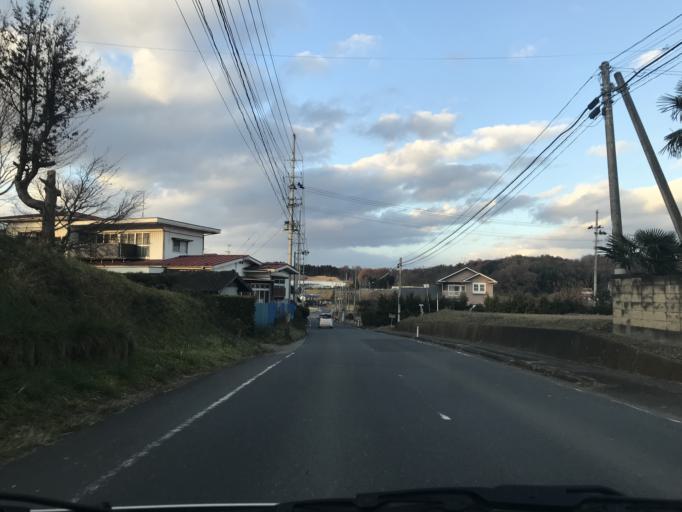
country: JP
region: Miyagi
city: Furukawa
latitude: 38.6625
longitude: 141.0113
